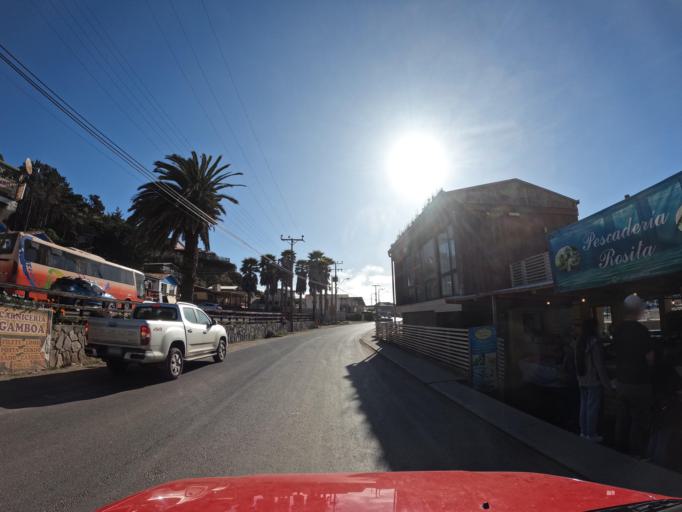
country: CL
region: Maule
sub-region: Provincia de Talca
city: Constitucion
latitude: -34.8858
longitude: -72.1662
